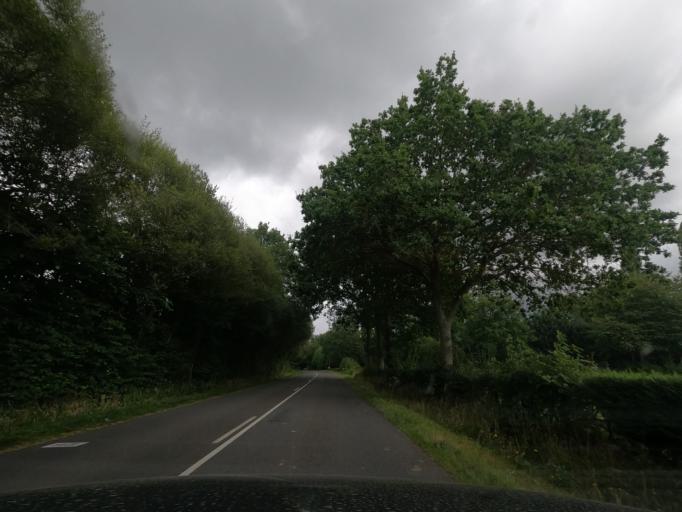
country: FR
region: Lower Normandy
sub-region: Departement de l'Orne
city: Briouze
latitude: 48.6885
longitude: -0.3911
